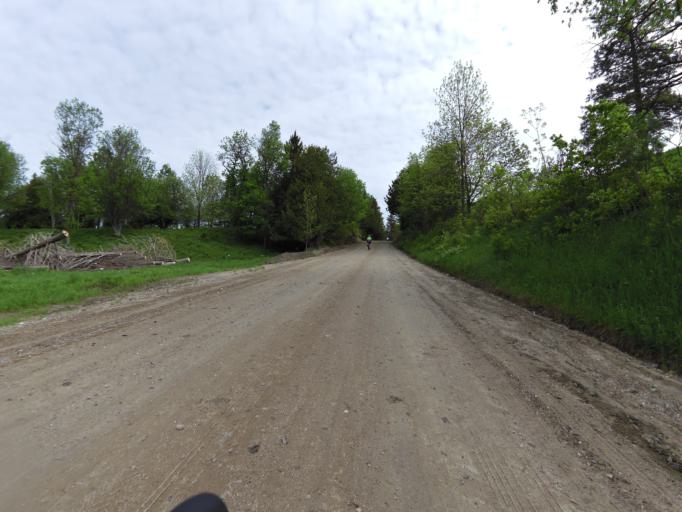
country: CA
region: Quebec
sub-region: Outaouais
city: Wakefield
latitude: 45.7319
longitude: -75.8903
